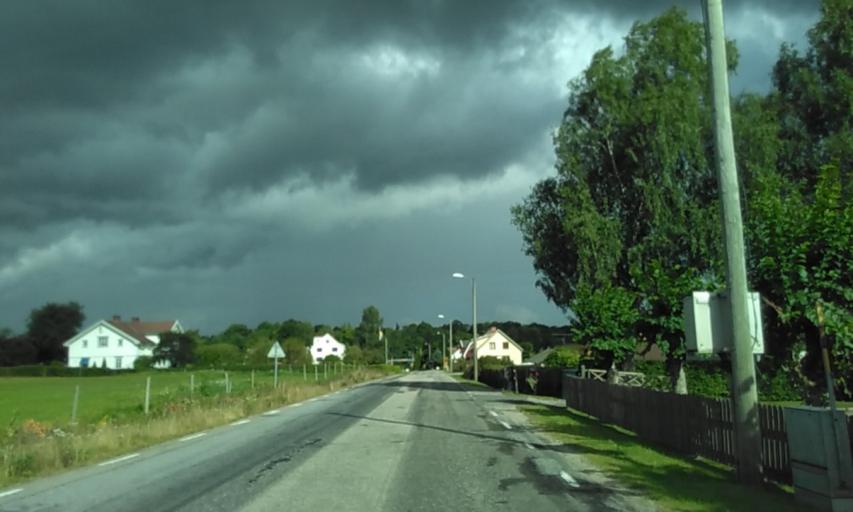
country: SE
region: Vaestra Goetaland
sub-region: Vargarda Kommun
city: Jonstorp
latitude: 58.0066
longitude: 12.7115
